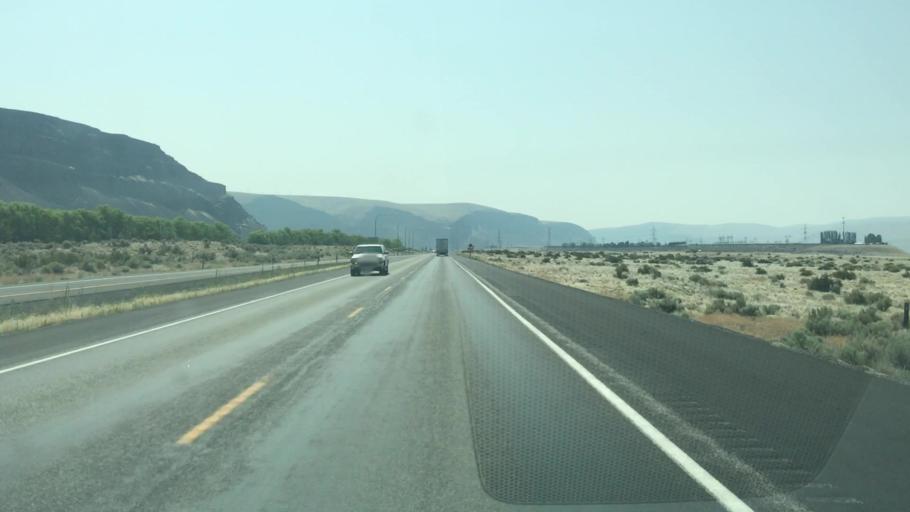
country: US
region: Washington
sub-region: Chelan County
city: South Wenatchee
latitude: 47.3184
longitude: -120.0728
